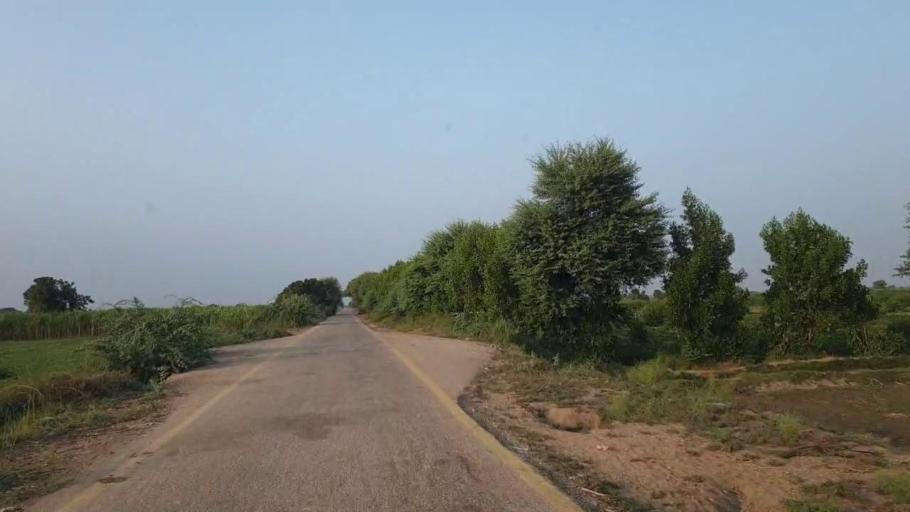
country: PK
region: Sindh
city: Tando Ghulam Ali
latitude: 25.0813
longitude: 68.9585
